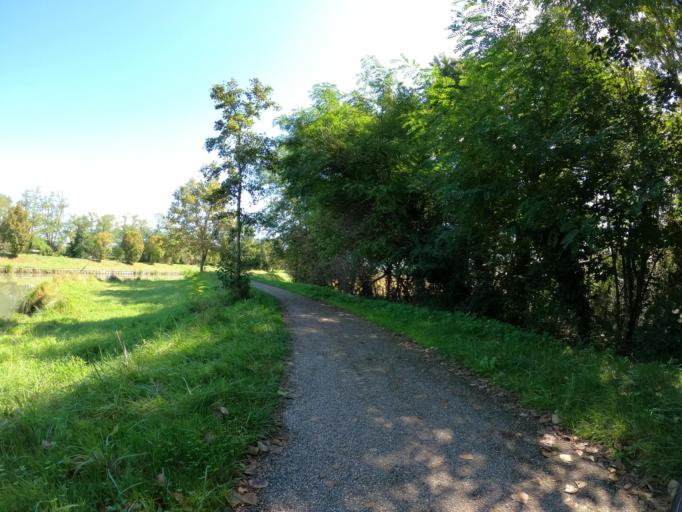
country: FR
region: Midi-Pyrenees
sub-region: Departement du Tarn-et-Garonne
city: Lamagistere
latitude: 44.1314
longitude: 0.8253
